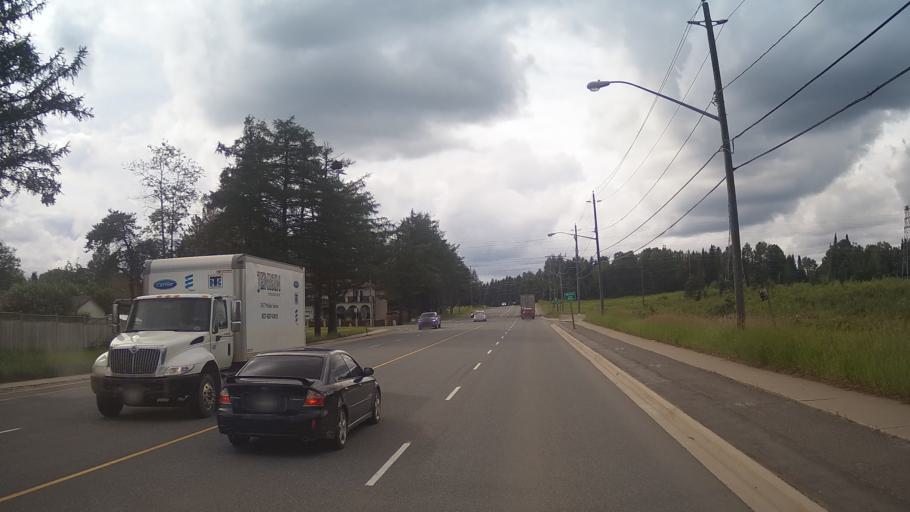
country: CA
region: Ontario
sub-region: Thunder Bay District
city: Thunder Bay
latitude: 48.4572
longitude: -89.2658
